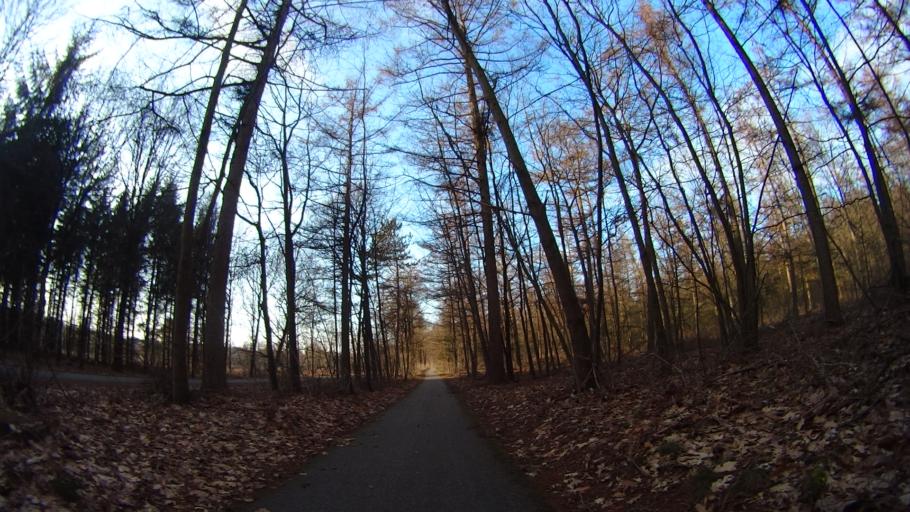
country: NL
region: Drenthe
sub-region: Gemeente Coevorden
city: Sleen
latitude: 52.8241
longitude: 6.7600
